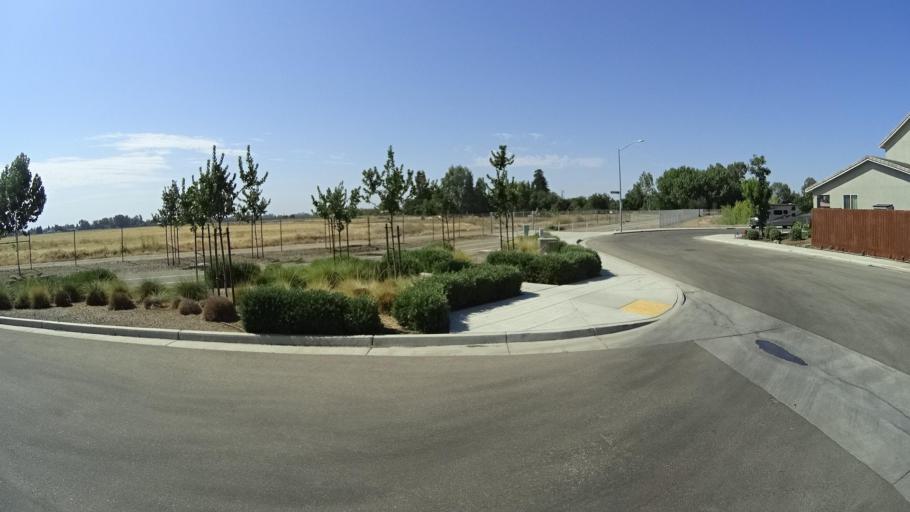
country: US
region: California
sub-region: Fresno County
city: Sunnyside
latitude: 36.7699
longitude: -119.6583
